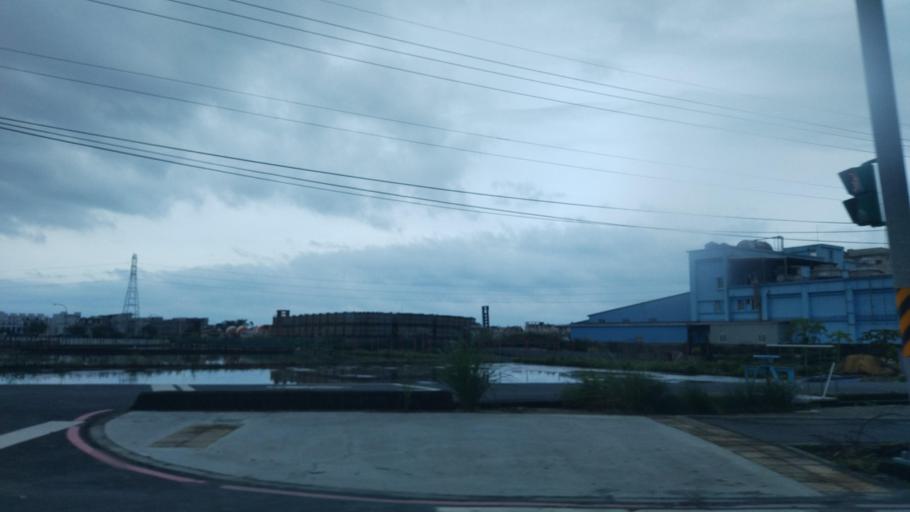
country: TW
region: Taiwan
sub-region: Yilan
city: Yilan
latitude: 24.6135
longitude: 121.8311
